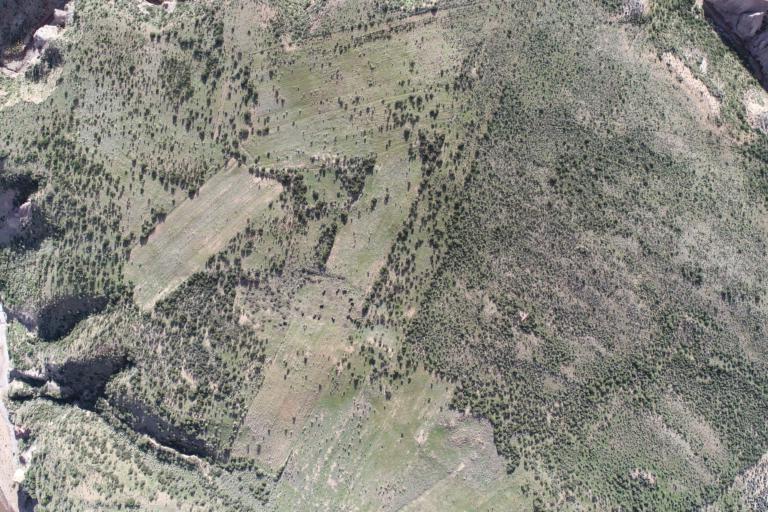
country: BO
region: La Paz
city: Patacamaya
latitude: -17.2981
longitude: -68.4885
